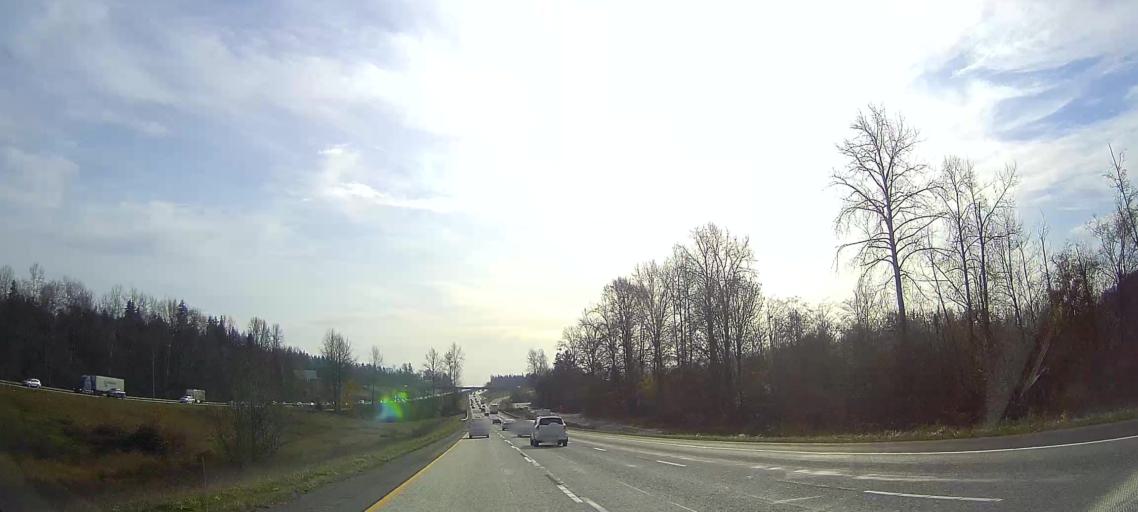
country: US
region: Washington
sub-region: Snohomish County
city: Bryant
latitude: 48.2166
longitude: -122.2195
